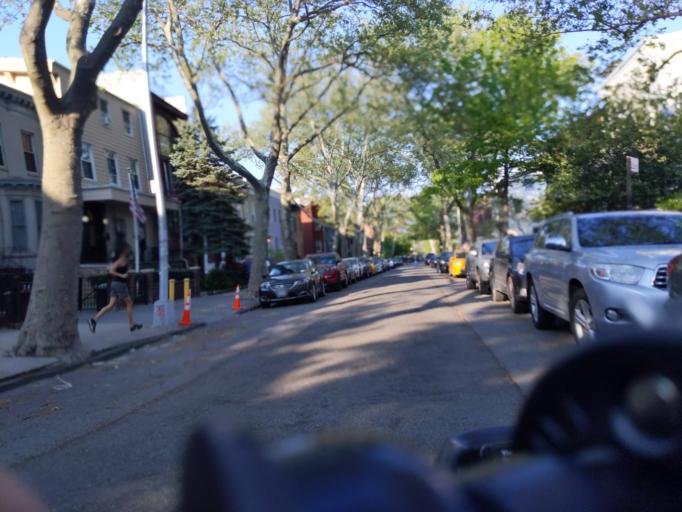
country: US
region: New York
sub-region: Queens County
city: Long Island City
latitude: 40.7148
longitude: -73.9406
